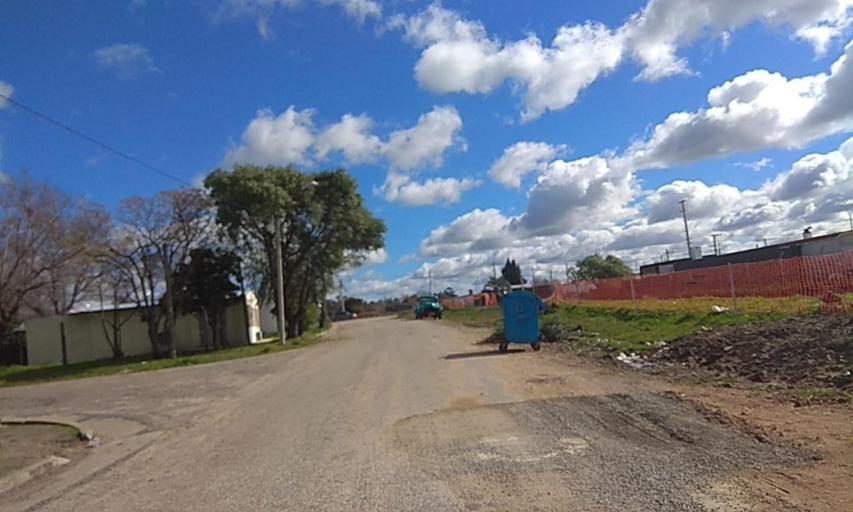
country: UY
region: Florida
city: Florida
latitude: -34.0795
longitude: -56.2219
